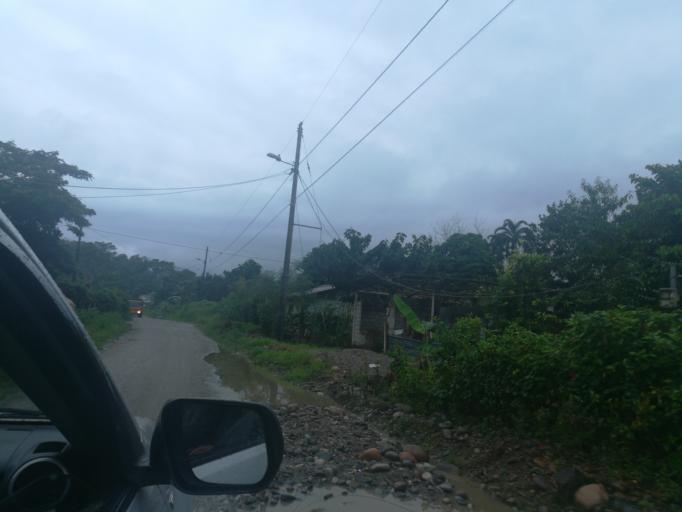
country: EC
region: Napo
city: Tena
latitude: -1.0385
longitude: -77.6605
